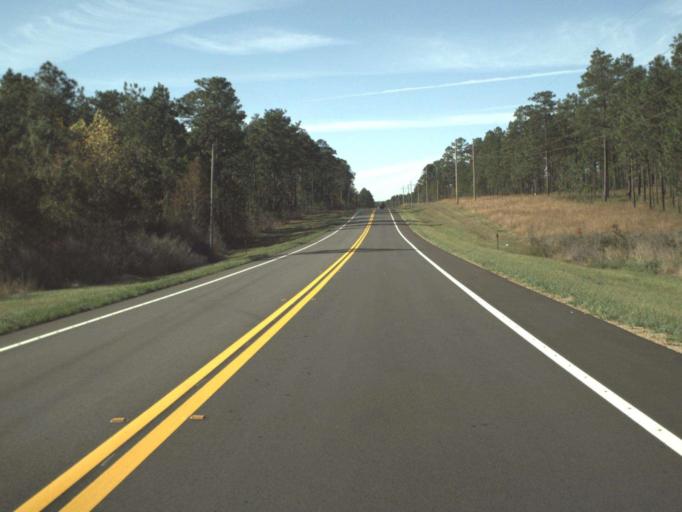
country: US
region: Florida
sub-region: Santa Rosa County
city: Point Baker
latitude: 30.8745
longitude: -86.9405
